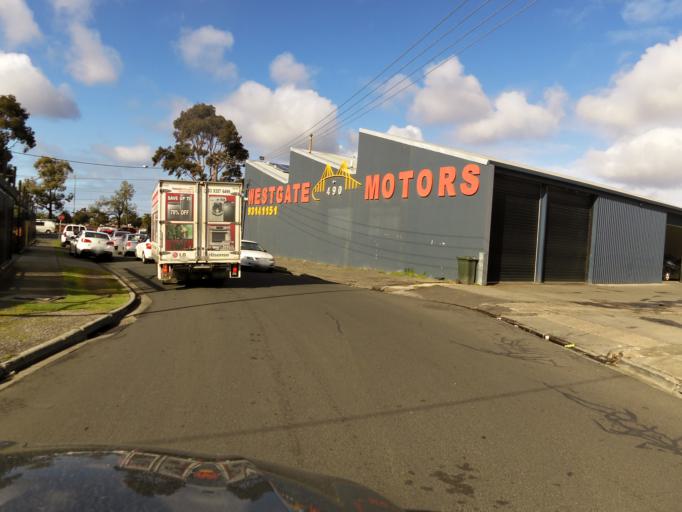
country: AU
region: Victoria
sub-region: Maribyrnong
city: Kingsville
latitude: -37.8126
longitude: 144.8612
